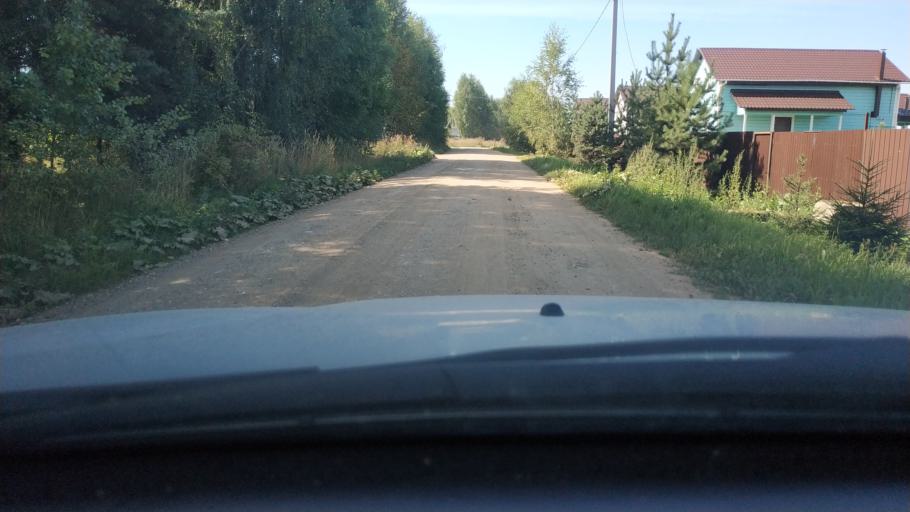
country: RU
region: Kostroma
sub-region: Kostromskoy Rayon
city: Kostroma
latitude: 57.7769
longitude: 40.7413
